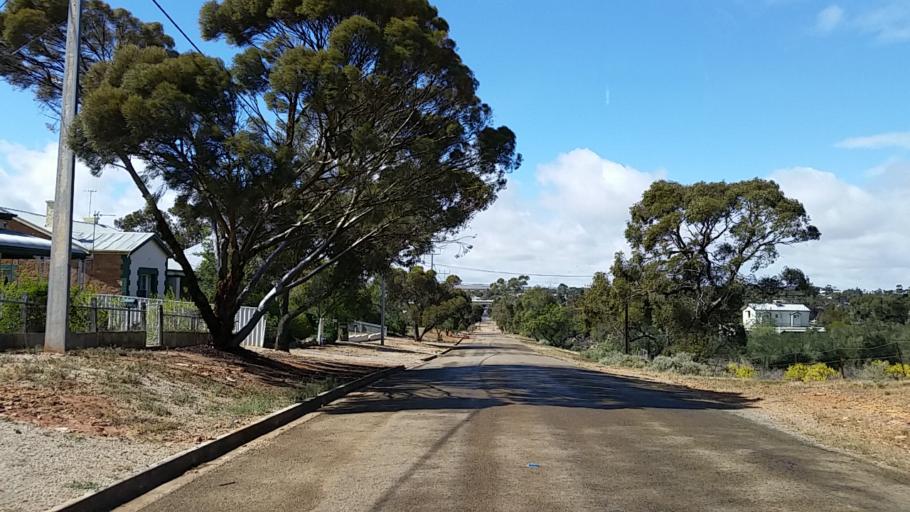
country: AU
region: South Australia
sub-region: Peterborough
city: Peterborough
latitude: -32.9680
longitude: 138.8358
